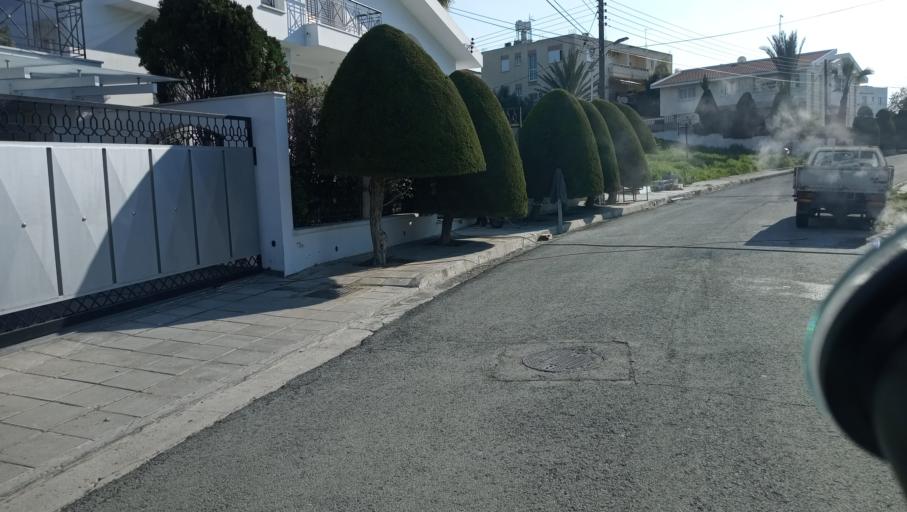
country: CY
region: Lefkosia
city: Nicosia
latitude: 35.1476
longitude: 33.3184
